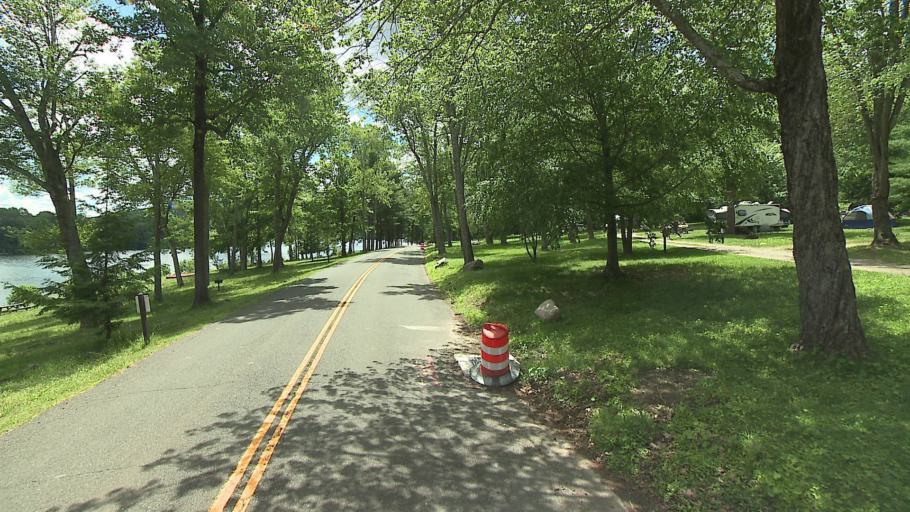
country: US
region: Connecticut
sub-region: Litchfield County
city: New Preston
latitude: 41.7044
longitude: -73.3810
